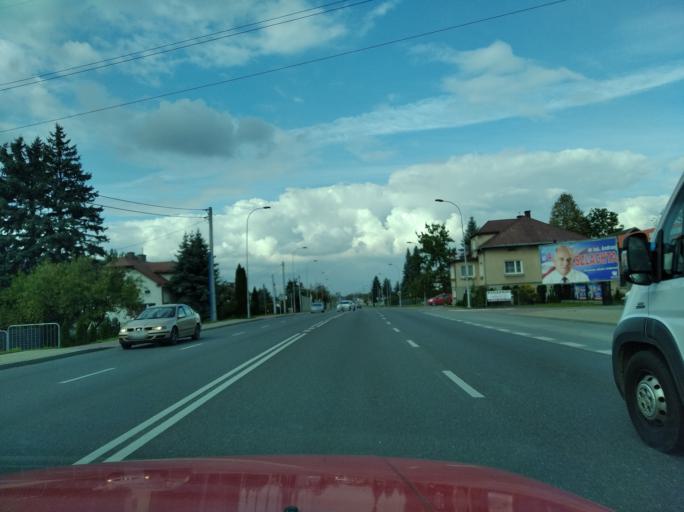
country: PL
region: Subcarpathian Voivodeship
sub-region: Powiat rzeszowski
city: Tyczyn
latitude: 49.9941
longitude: 22.0181
